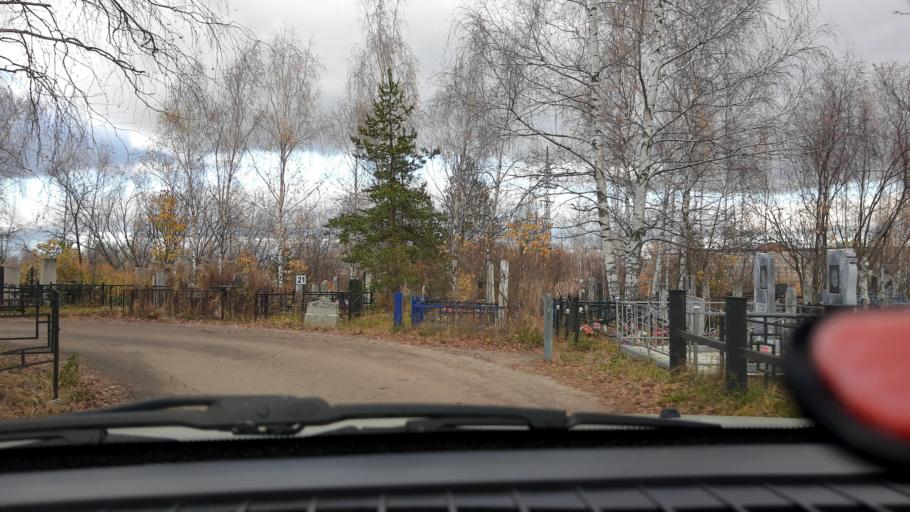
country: RU
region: Nizjnij Novgorod
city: Gorbatovka
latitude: 56.3605
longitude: 43.7873
